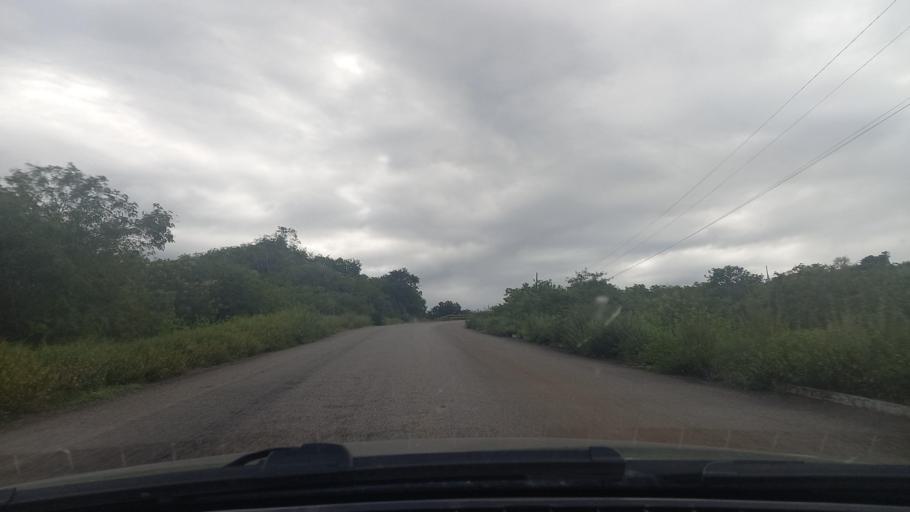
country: BR
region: Sergipe
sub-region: Caninde De Sao Francisco
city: Caninde de Sao Francisco
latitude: -9.6318
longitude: -37.7834
